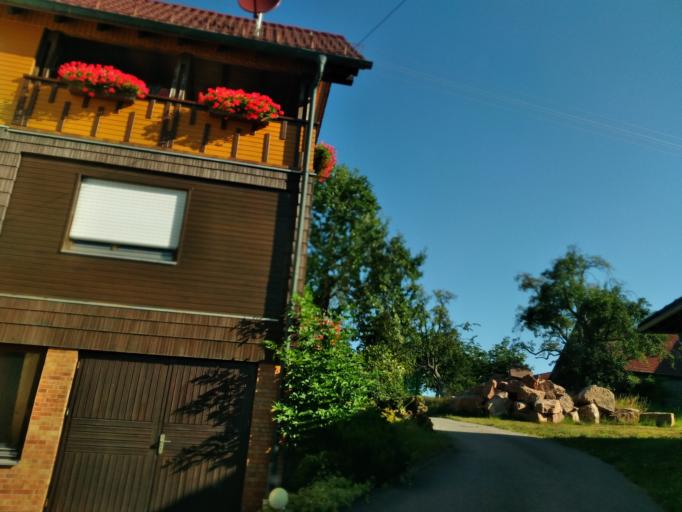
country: DE
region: Baden-Wuerttemberg
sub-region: Karlsruhe Region
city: Limbach
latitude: 49.4828
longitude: 9.2118
